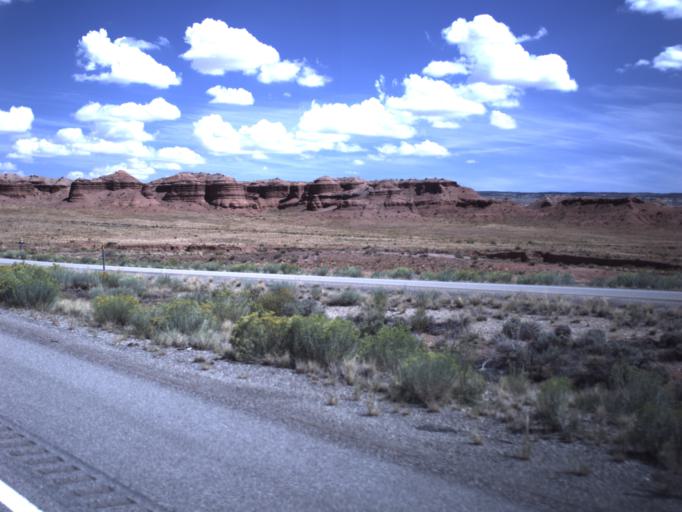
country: US
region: Utah
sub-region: Emery County
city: Ferron
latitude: 38.8430
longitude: -111.0629
